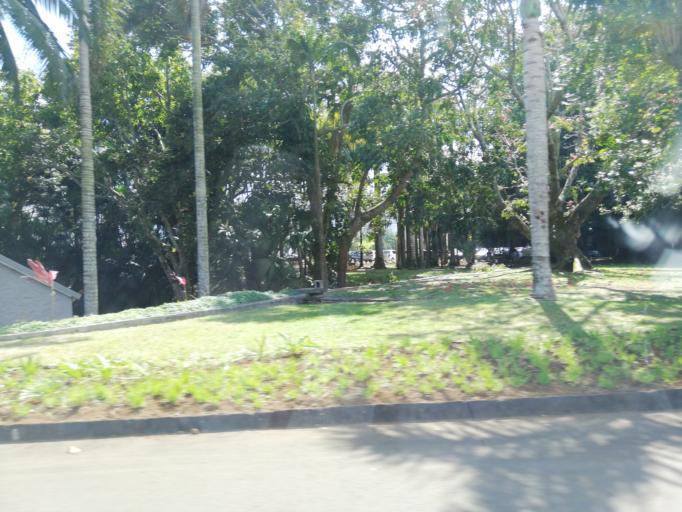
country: MU
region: Moka
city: Verdun
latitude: -20.2255
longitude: 57.5331
